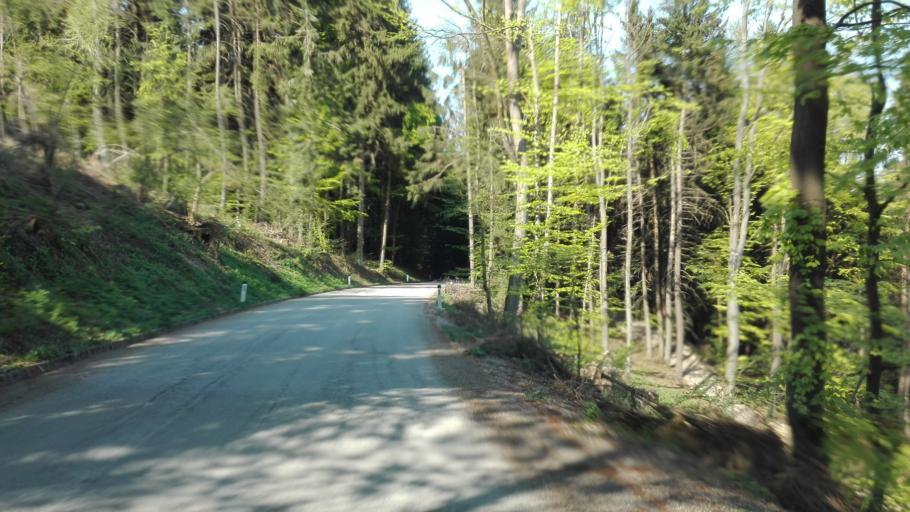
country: AT
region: Upper Austria
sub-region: Politischer Bezirk Rohrbach
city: Atzesberg
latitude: 48.4208
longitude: 13.9181
